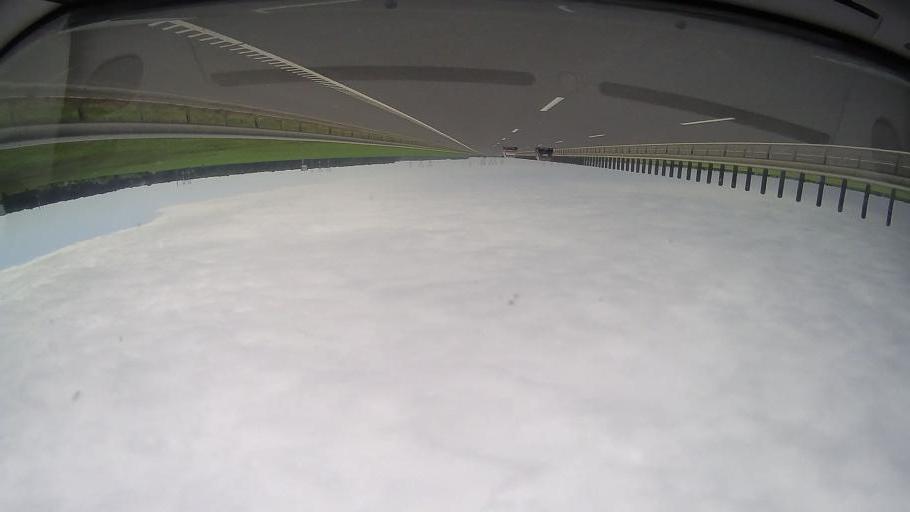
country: RO
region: Ilfov
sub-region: Comuna Tunari
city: Tunari
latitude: 44.5645
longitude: 26.1815
